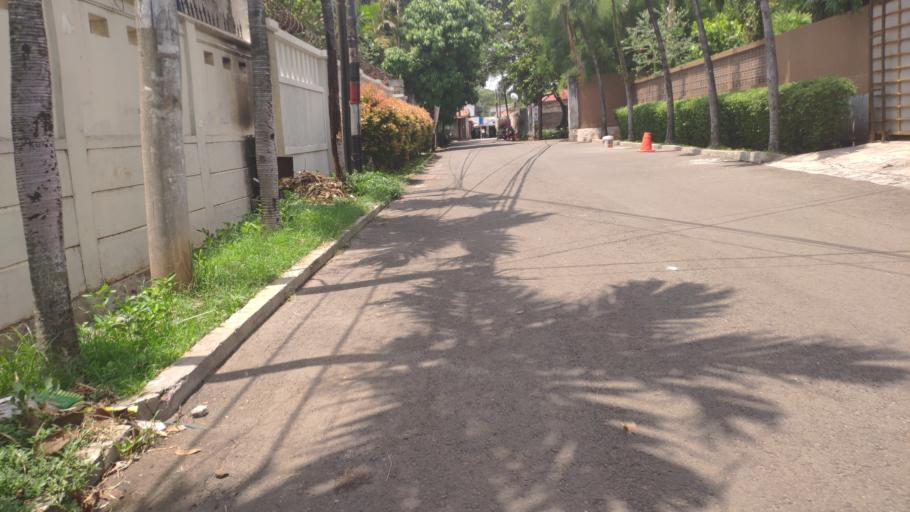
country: ID
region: Jakarta Raya
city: Jakarta
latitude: -6.2695
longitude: 106.8269
